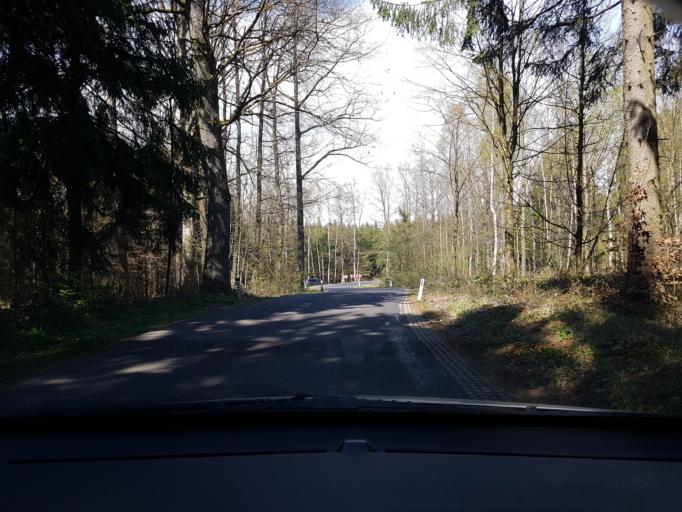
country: AT
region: Upper Austria
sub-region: Politischer Bezirk Linz-Land
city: Ansfelden
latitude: 48.2011
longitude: 14.3294
